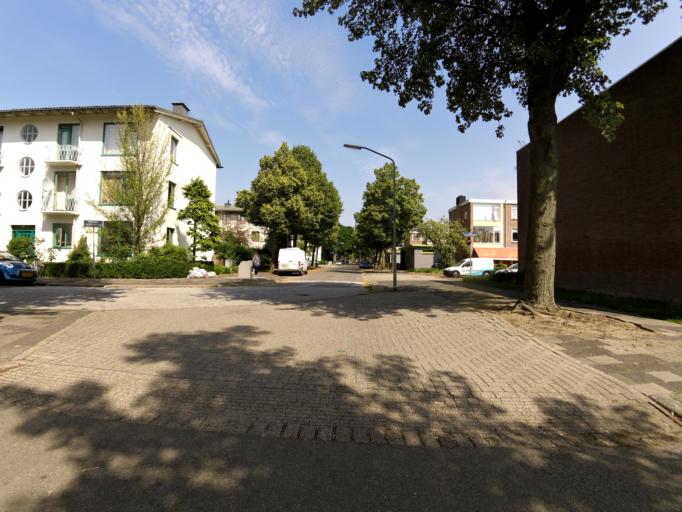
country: NL
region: South Holland
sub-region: Gemeente Dordrecht
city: Dordrecht
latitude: 51.7986
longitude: 4.6676
